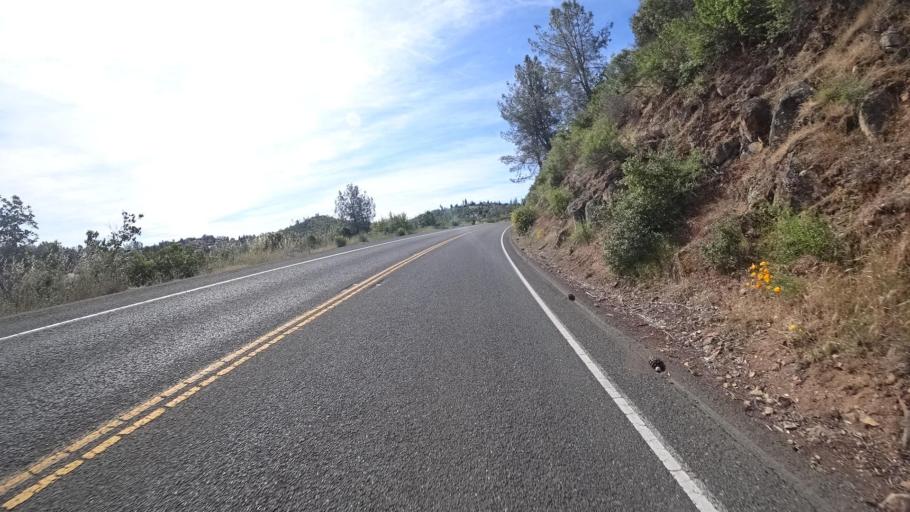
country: US
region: California
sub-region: Lake County
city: Soda Bay
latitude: 38.9601
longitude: -122.7292
